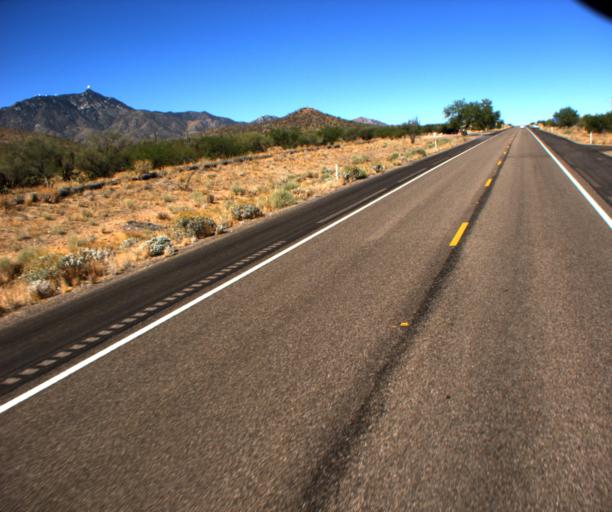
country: US
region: Arizona
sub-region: Pima County
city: Three Points
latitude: 32.0349
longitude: -111.5461
